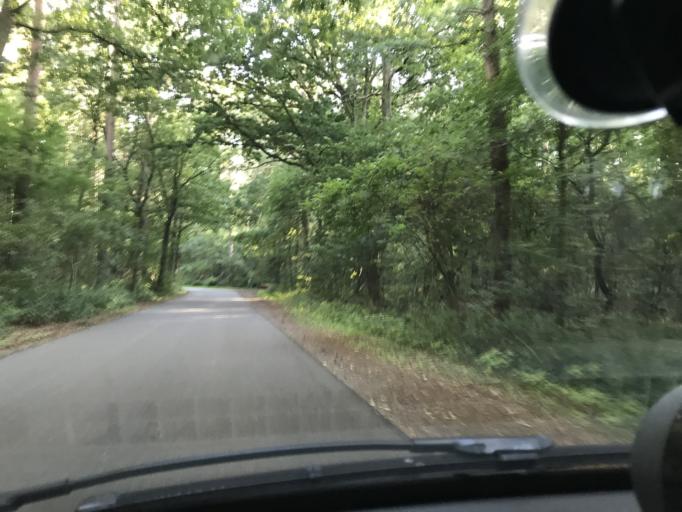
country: DE
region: Lower Saxony
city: Buxtehude
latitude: 53.4535
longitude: 9.7286
